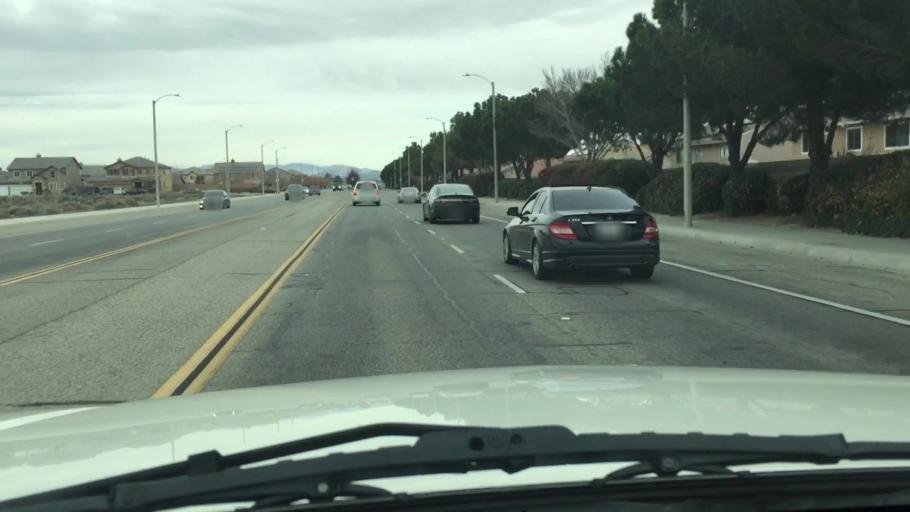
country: US
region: California
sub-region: Los Angeles County
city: Lancaster
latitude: 34.6915
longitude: -118.1838
